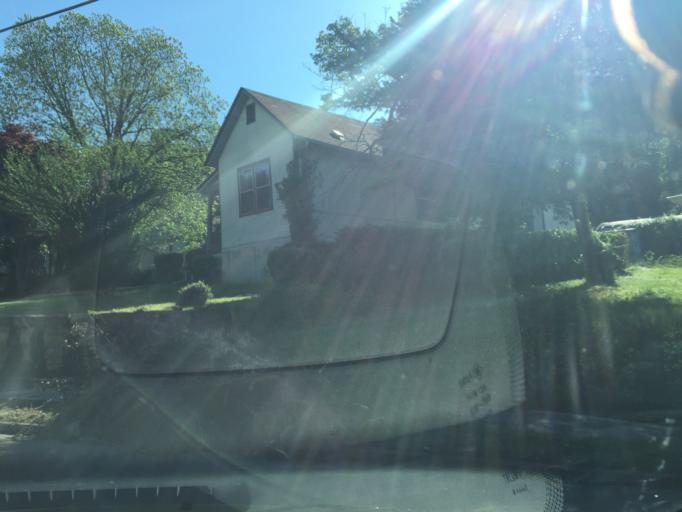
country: US
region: Tennessee
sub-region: Hamilton County
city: Lookout Mountain
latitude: 34.9985
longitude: -85.3278
